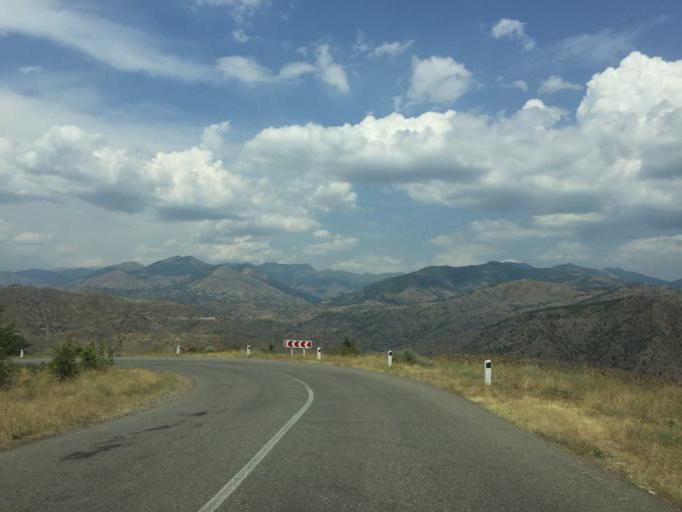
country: AZ
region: Lacin
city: Lacin
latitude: 39.5781
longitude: 46.5439
